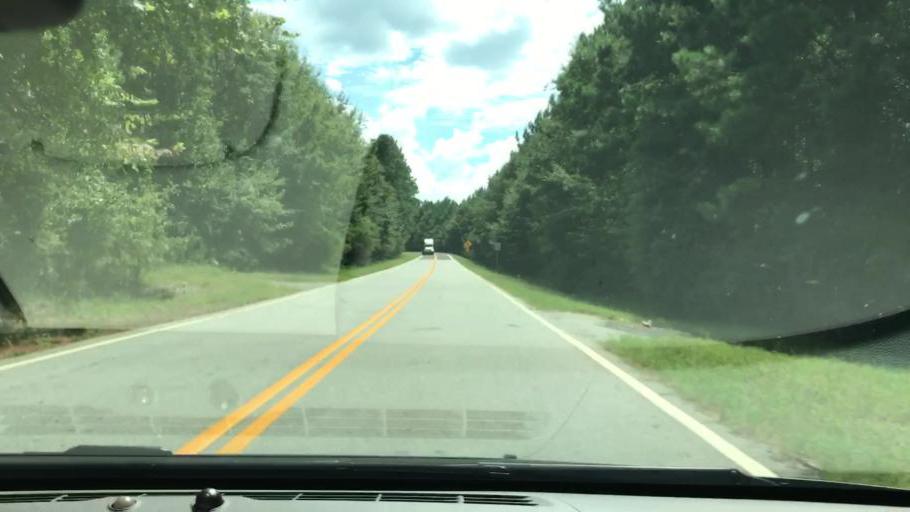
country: US
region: Georgia
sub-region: Quitman County
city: Georgetown
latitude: 31.9844
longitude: -85.0499
